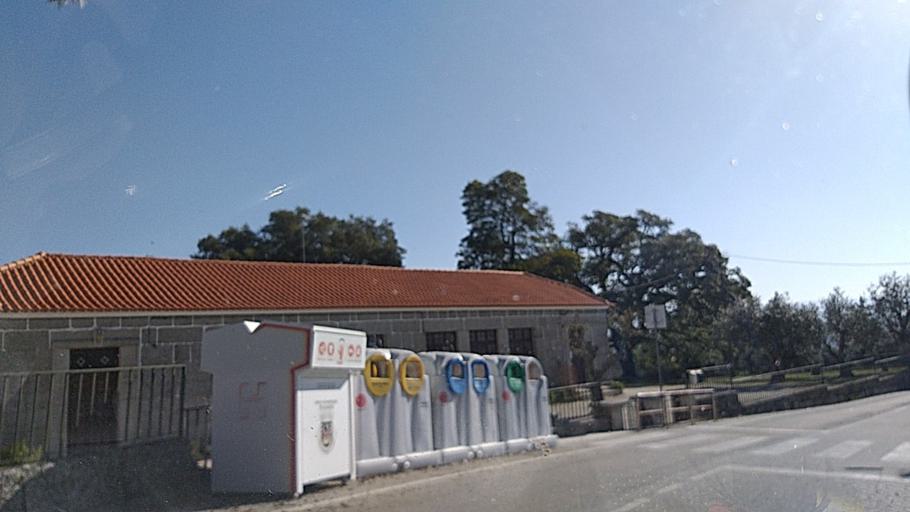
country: PT
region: Guarda
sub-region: Celorico da Beira
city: Celorico da Beira
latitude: 40.6725
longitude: -7.3959
